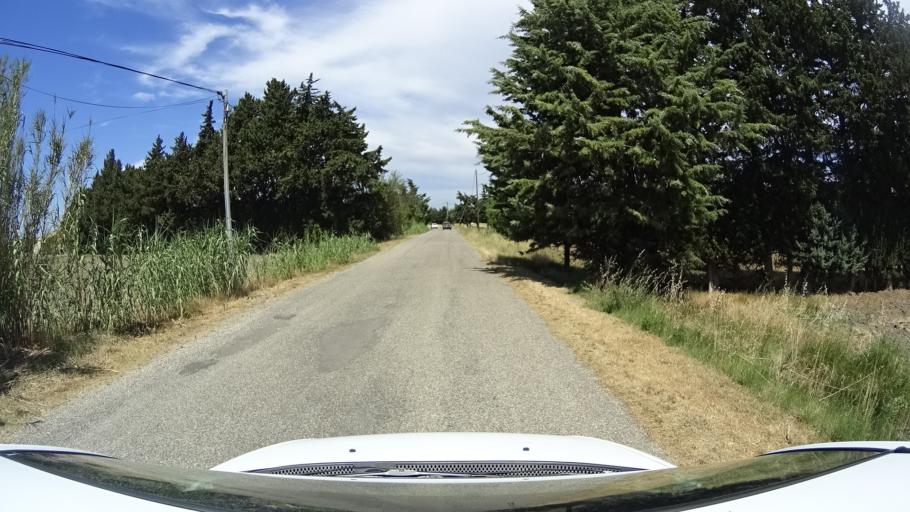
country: FR
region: Provence-Alpes-Cote d'Azur
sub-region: Departement du Vaucluse
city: Cheval-Blanc
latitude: 43.8185
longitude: 5.0594
